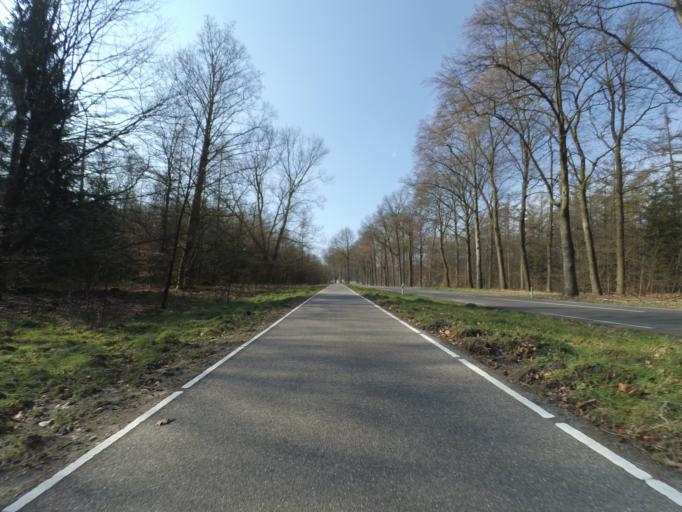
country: NL
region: Gelderland
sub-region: Gemeente Apeldoorn
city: Beekbergen
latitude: 52.1547
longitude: 5.8903
